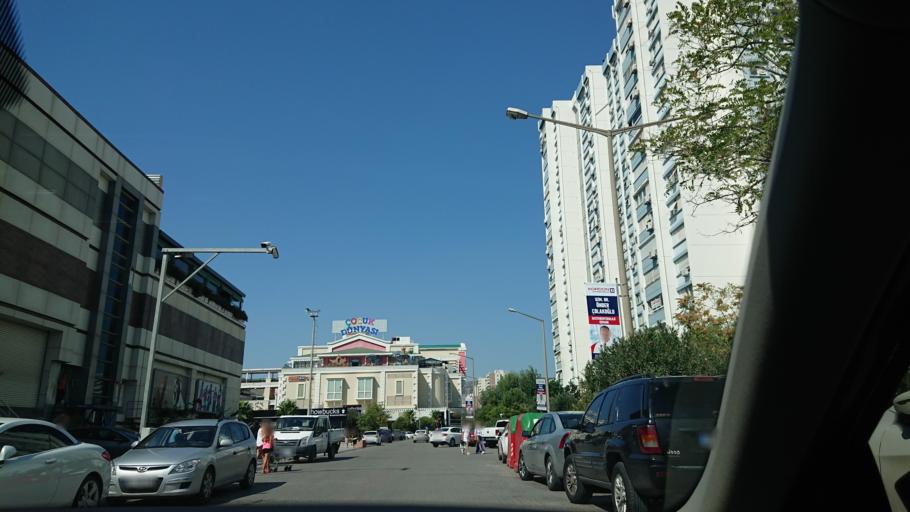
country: TR
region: Izmir
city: Karsiyaka
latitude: 38.4710
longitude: 27.0755
